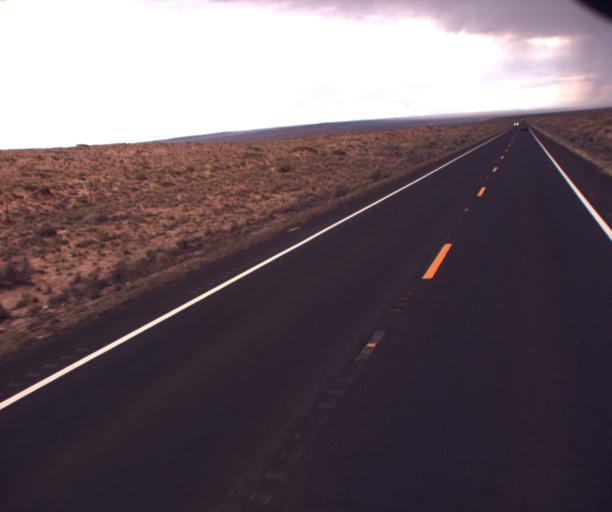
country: US
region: Arizona
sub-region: Coconino County
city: Tuba City
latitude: 36.2151
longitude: -111.0457
